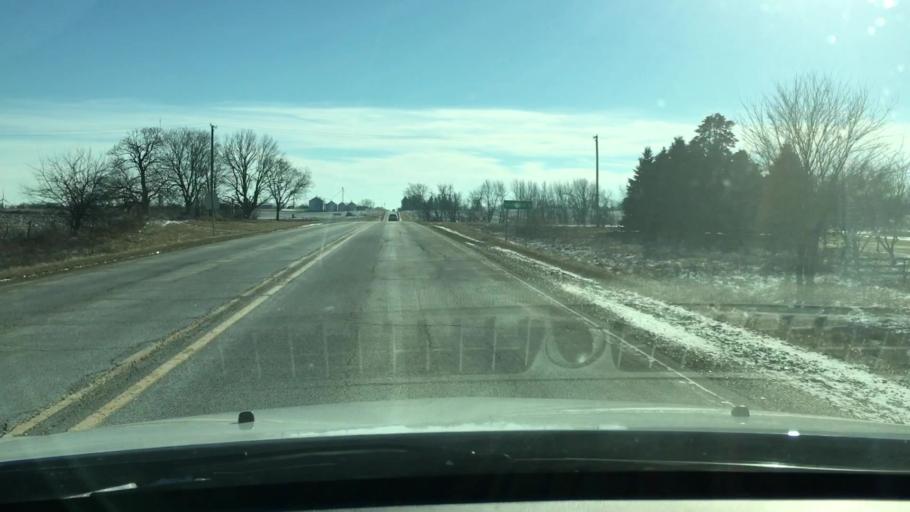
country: US
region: Illinois
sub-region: LaSalle County
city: Mendota
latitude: 41.7079
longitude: -89.0915
